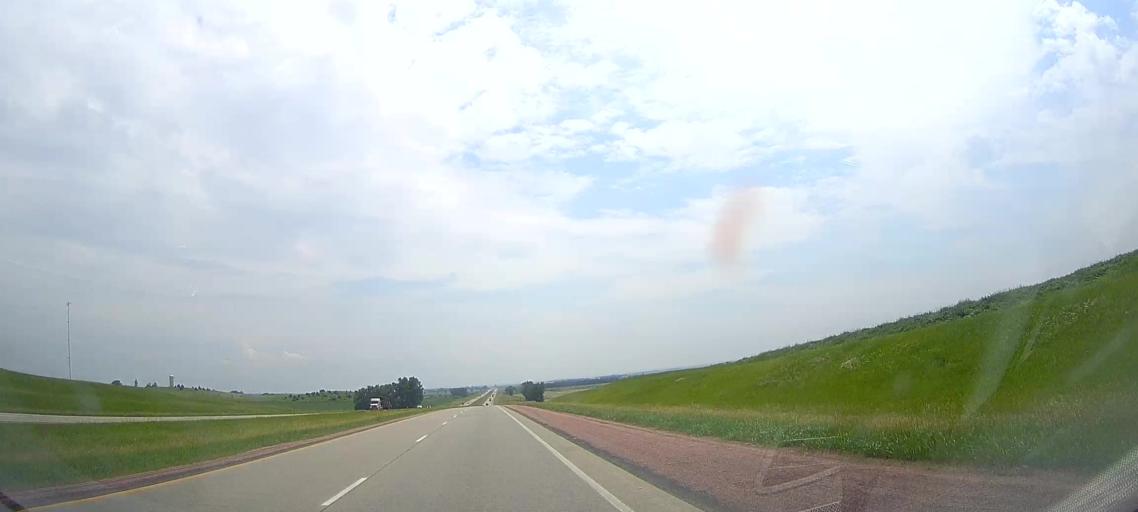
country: US
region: South Dakota
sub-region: Clay County
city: Vermillion
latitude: 42.9007
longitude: -96.7951
